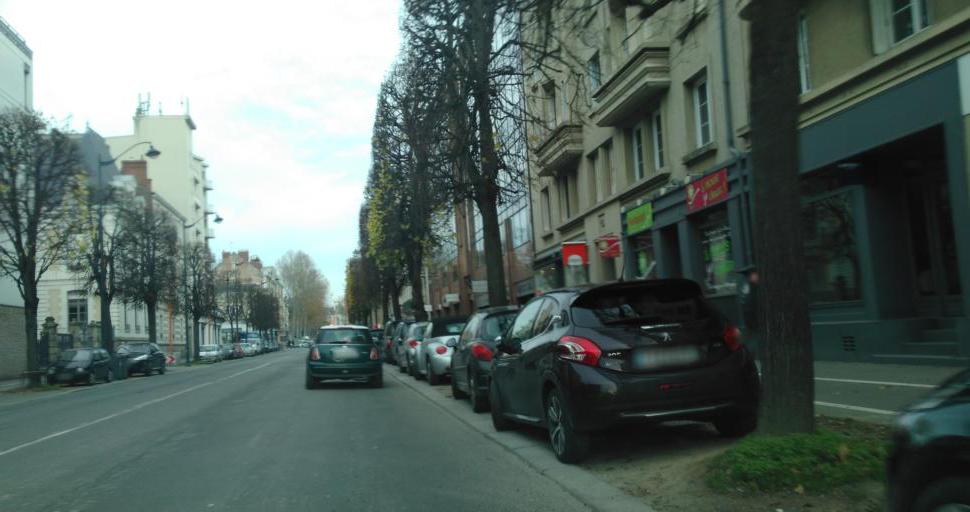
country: FR
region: Brittany
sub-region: Departement d'Ille-et-Vilaine
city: Rennes
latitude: 48.1070
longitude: -1.6845
